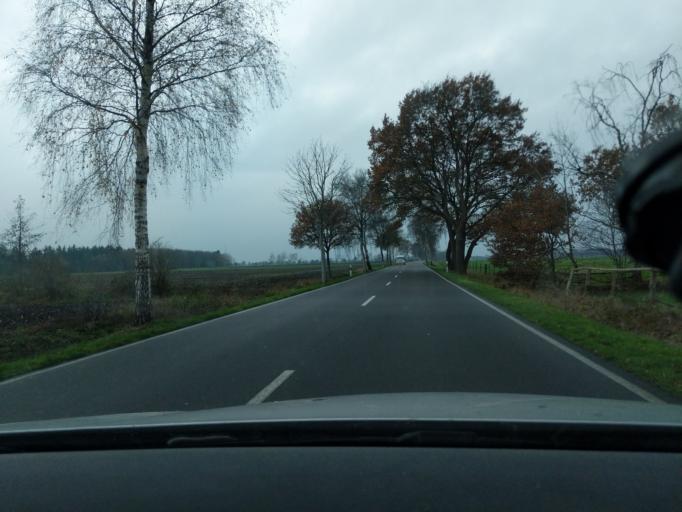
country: DE
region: Lower Saxony
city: Ahlerstedt
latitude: 53.3735
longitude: 9.4488
